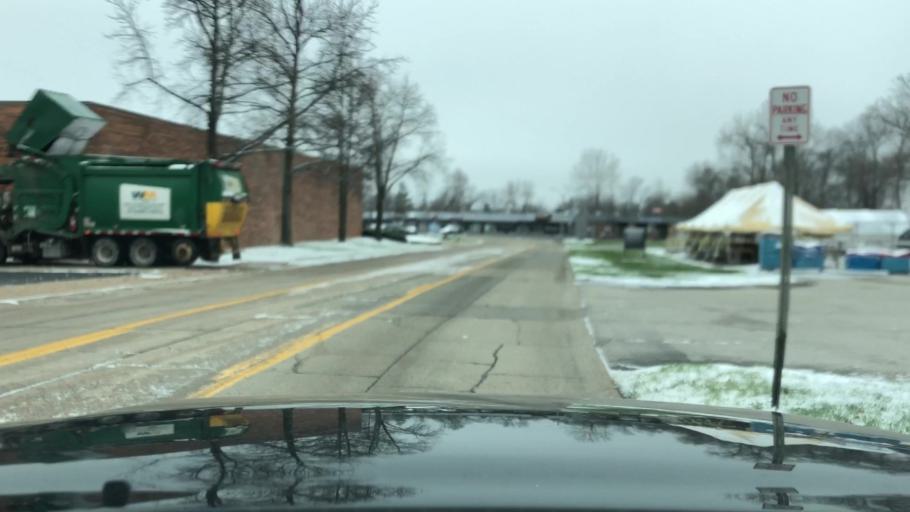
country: US
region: Missouri
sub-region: Saint Charles County
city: Saint Charles
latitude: 38.7885
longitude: -90.5141
